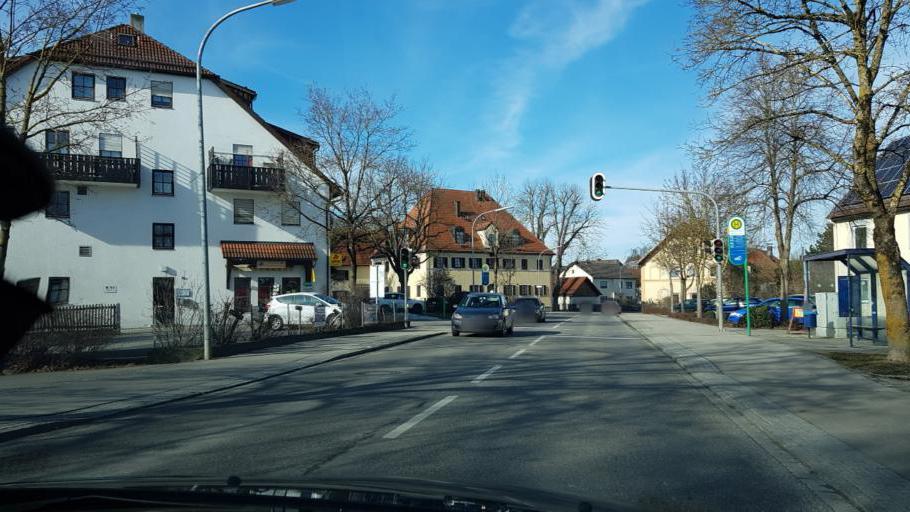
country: DE
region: Bavaria
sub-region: Upper Bavaria
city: Mammendorf
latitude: 48.2077
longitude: 11.1647
